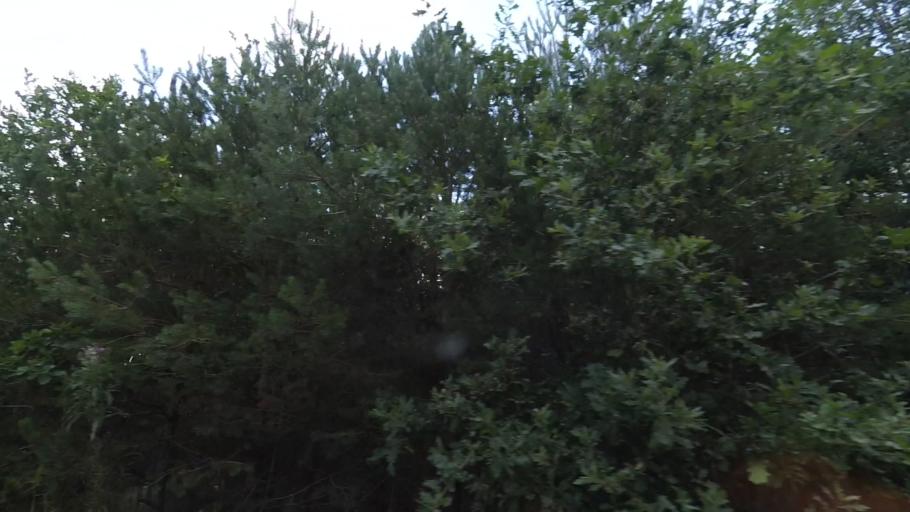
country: DK
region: Central Jutland
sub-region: Norddjurs Kommune
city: Allingabro
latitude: 56.4952
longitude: 10.3696
